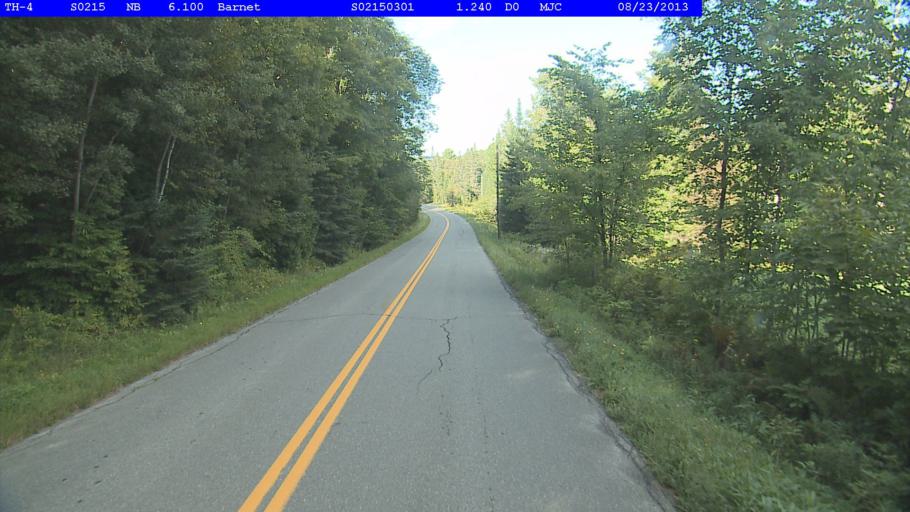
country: US
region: New Hampshire
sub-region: Grafton County
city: Woodsville
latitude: 44.2906
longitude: -72.1658
